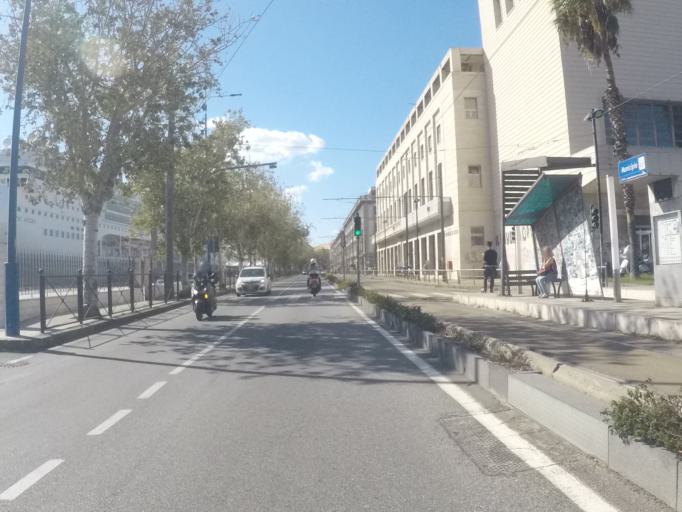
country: IT
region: Sicily
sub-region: Messina
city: Messina
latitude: 38.1938
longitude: 15.5574
